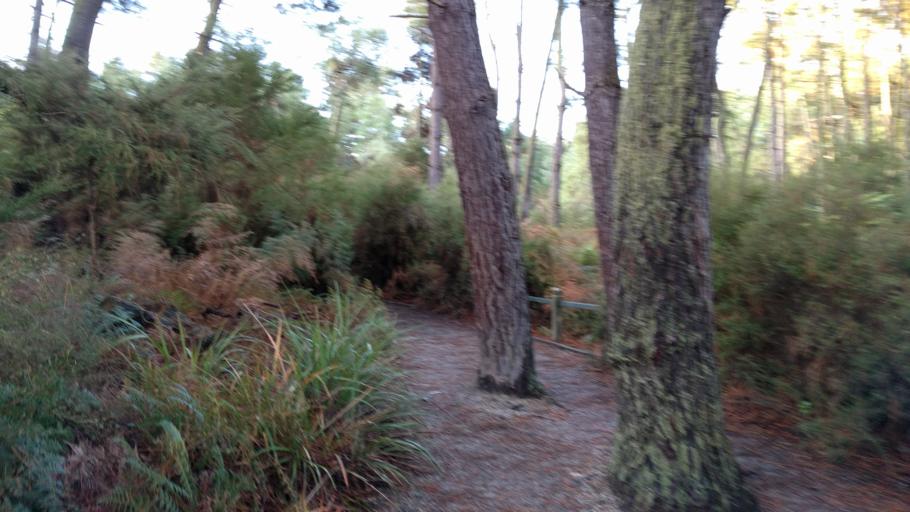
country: NZ
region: Bay of Plenty
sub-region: Rotorua District
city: Rotorua
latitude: -38.3619
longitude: 176.3704
